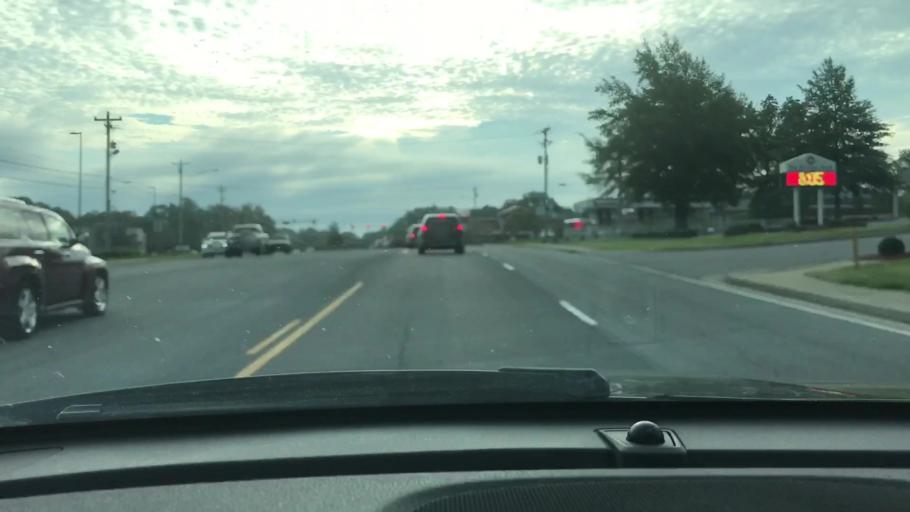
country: US
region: Tennessee
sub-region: Sumner County
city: White House
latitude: 36.4689
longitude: -86.6673
